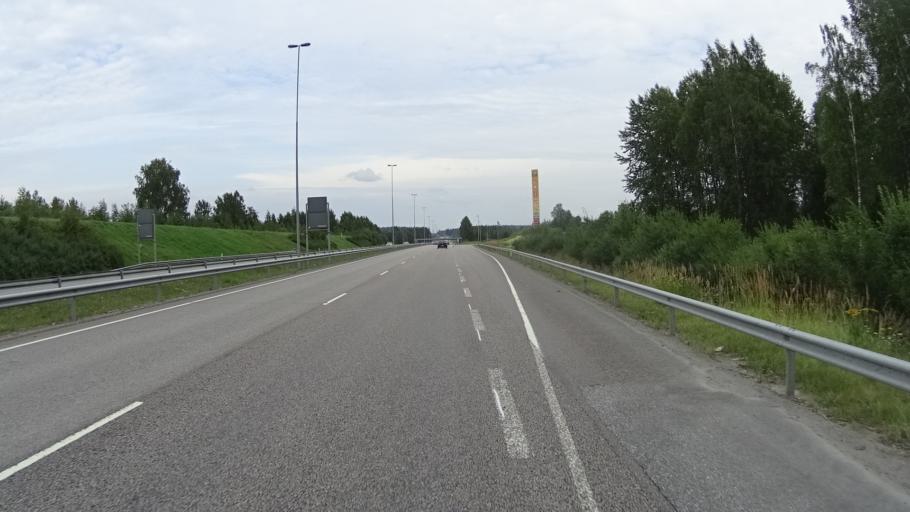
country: FI
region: South Karelia
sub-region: Lappeenranta
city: Lappeenranta
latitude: 61.0521
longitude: 28.2497
